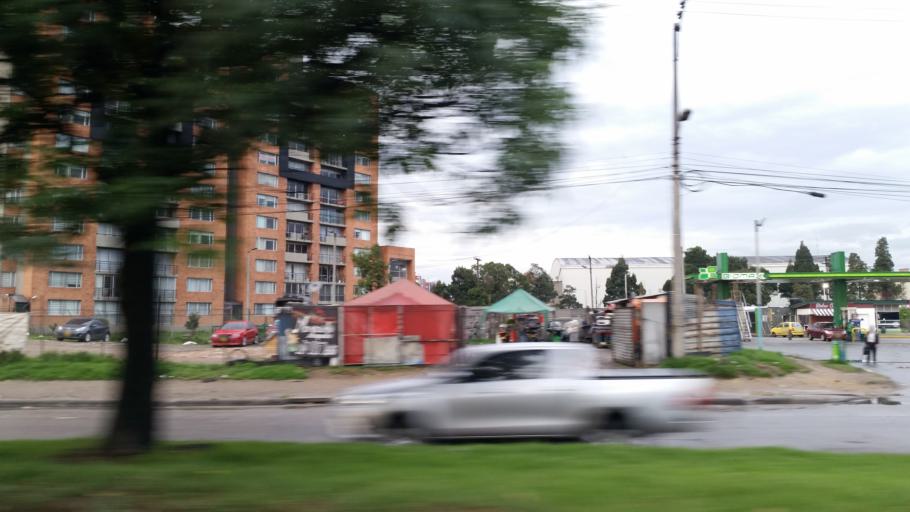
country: CO
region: Bogota D.C.
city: Bogota
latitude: 4.6622
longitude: -74.1384
